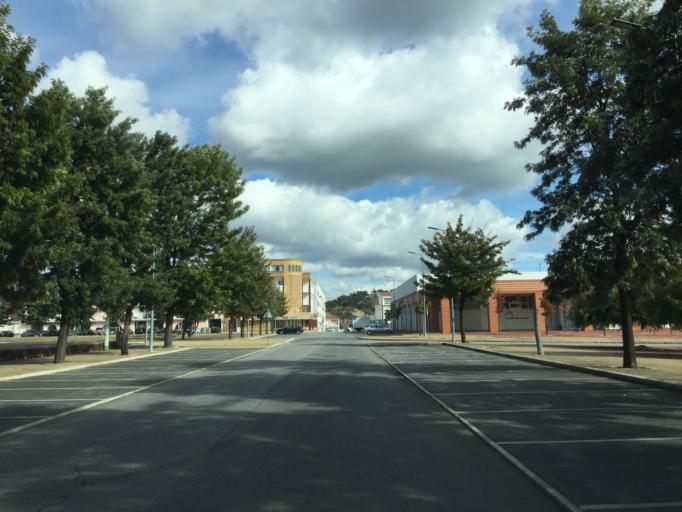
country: PT
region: Portalegre
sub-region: Ponte de Sor
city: Ponte de Sor
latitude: 39.2528
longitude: -8.0124
